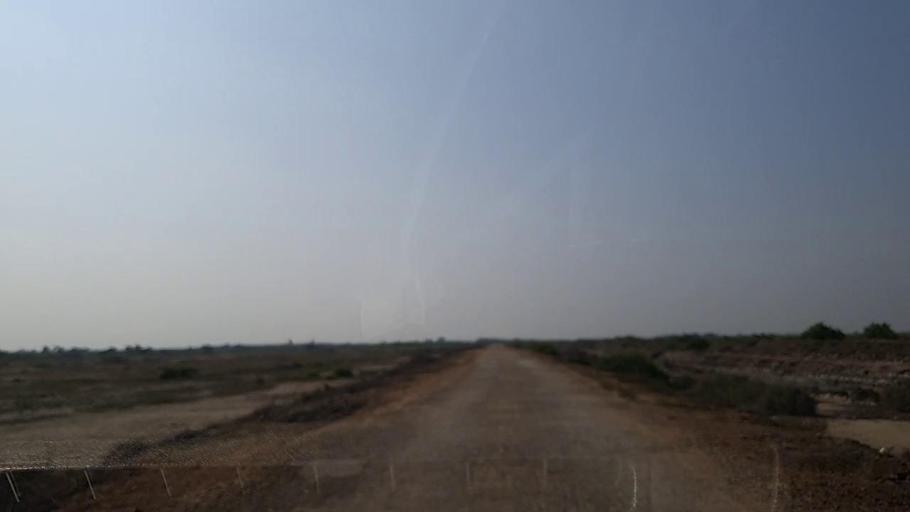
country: PK
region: Sindh
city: Mirpur Sakro
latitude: 24.6348
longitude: 67.7196
